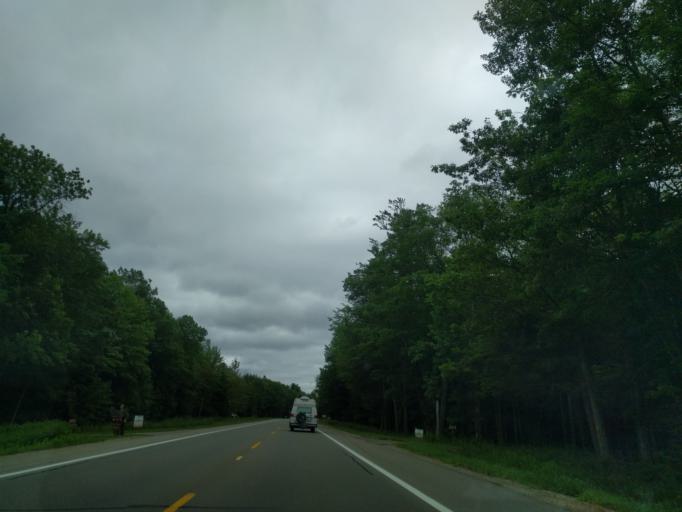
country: US
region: Michigan
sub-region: Menominee County
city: Menominee
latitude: 45.3023
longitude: -87.4396
